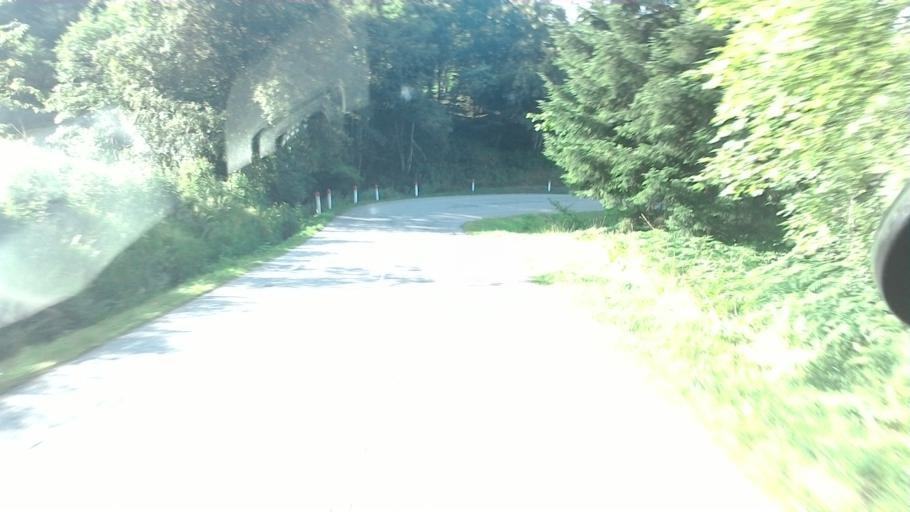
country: FR
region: Lorraine
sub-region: Departement des Vosges
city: Rupt-sur-Moselle
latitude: 47.9090
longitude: 6.6462
